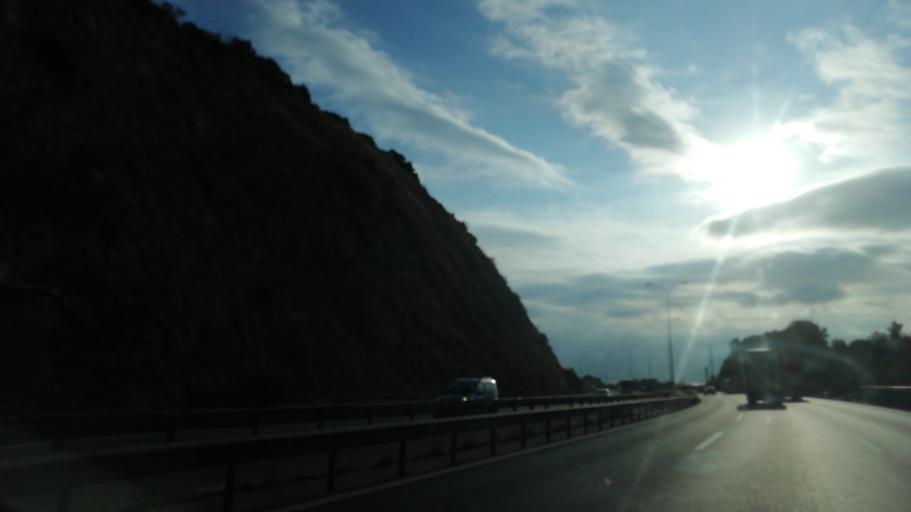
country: TR
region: Kocaeli
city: Hereke
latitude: 40.7789
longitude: 29.6305
